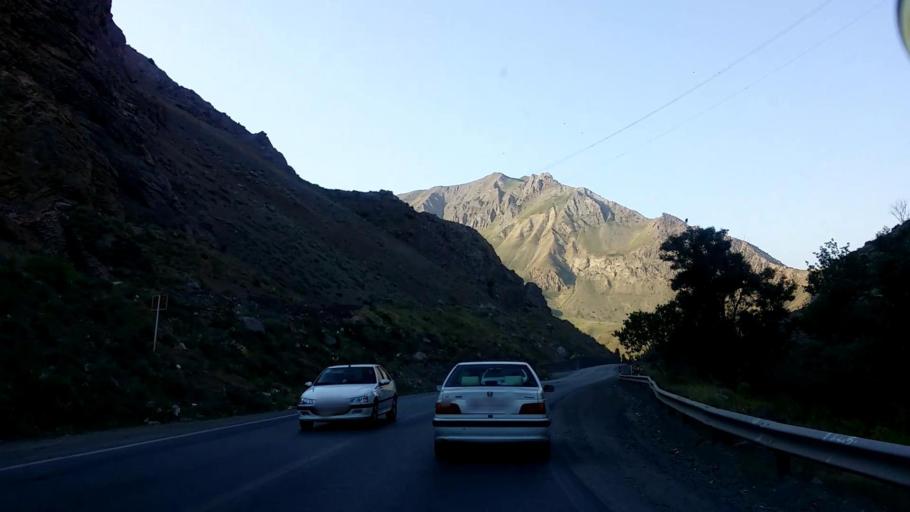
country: IR
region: Tehran
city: Tajrish
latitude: 36.0891
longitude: 51.3154
